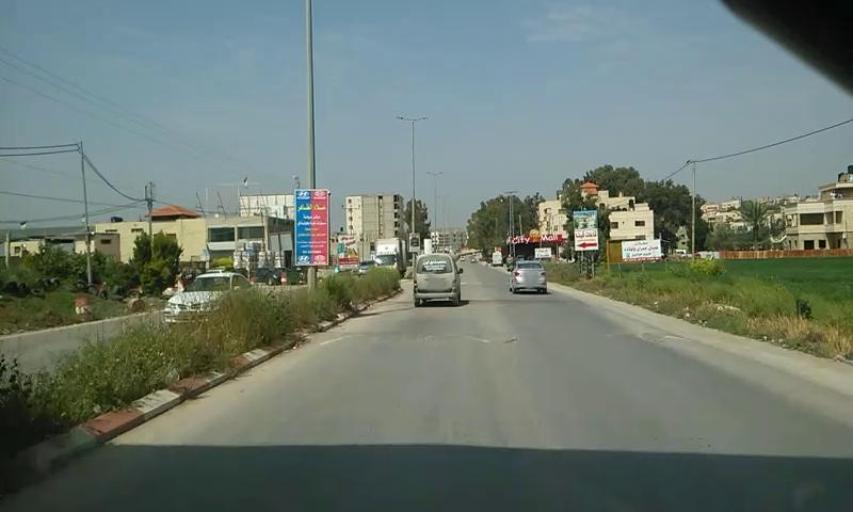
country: PS
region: West Bank
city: Janin
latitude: 32.4770
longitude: 35.3007
